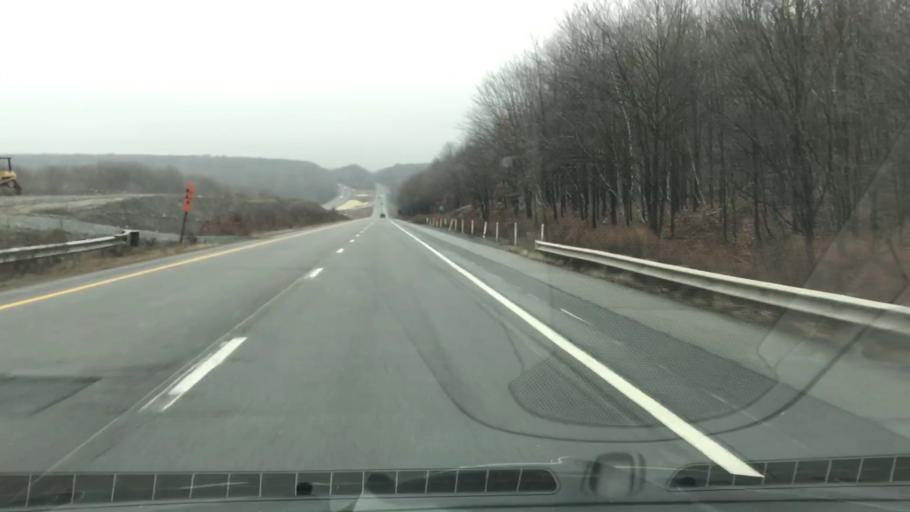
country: US
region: Pennsylvania
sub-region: Pike County
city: Hemlock Farms
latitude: 41.3474
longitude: -75.0005
